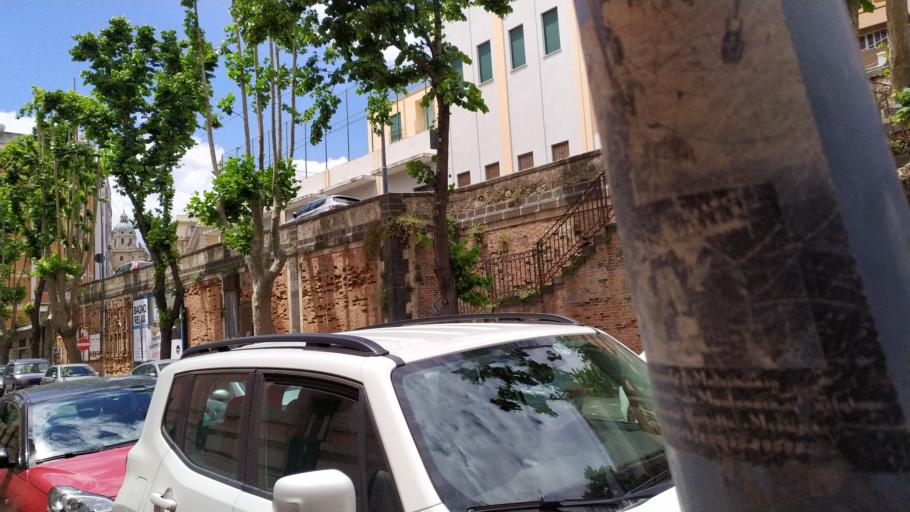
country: IT
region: Sicily
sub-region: Messina
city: Messina
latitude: 38.2002
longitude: 15.5555
